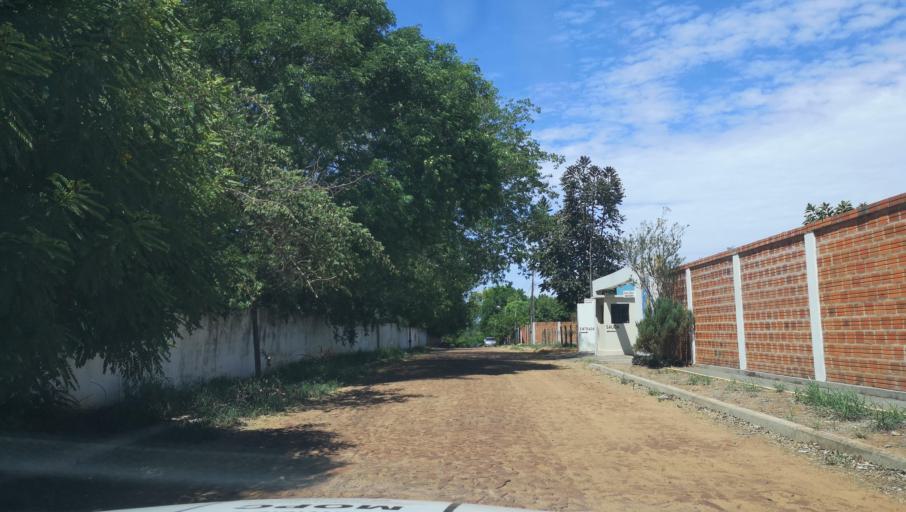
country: PY
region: Misiones
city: Santa Maria
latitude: -26.8788
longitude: -57.0291
